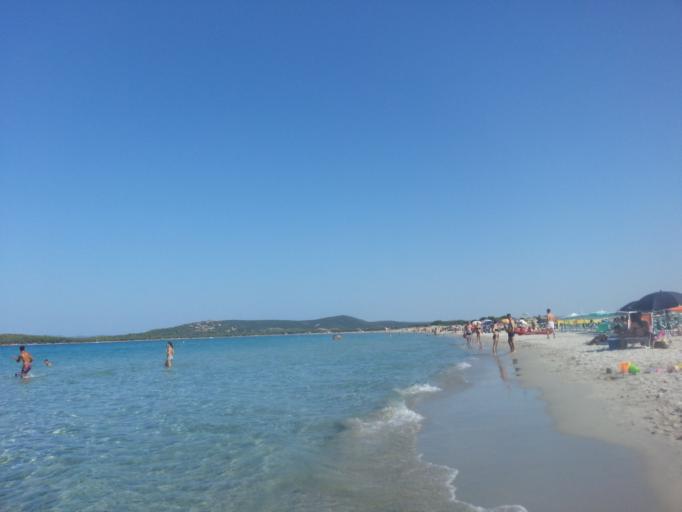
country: IT
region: Sardinia
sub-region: Provincia di Carbonia-Iglesias
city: Sant'Anna Arresi
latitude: 38.9535
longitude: 8.6161
